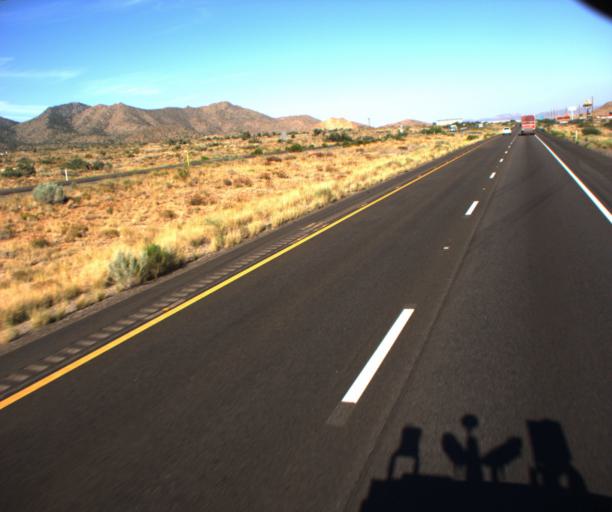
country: US
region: Arizona
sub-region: Mohave County
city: New Kingman-Butler
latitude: 35.1973
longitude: -113.8928
